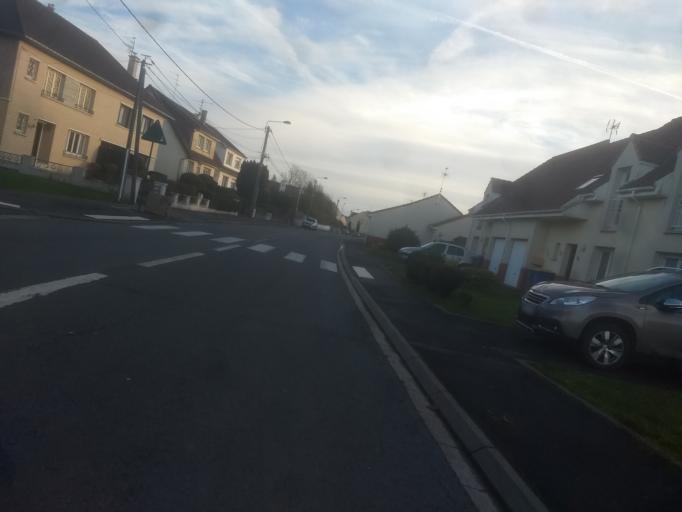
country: FR
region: Nord-Pas-de-Calais
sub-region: Departement du Pas-de-Calais
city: Beaurains
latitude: 50.2668
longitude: 2.7899
